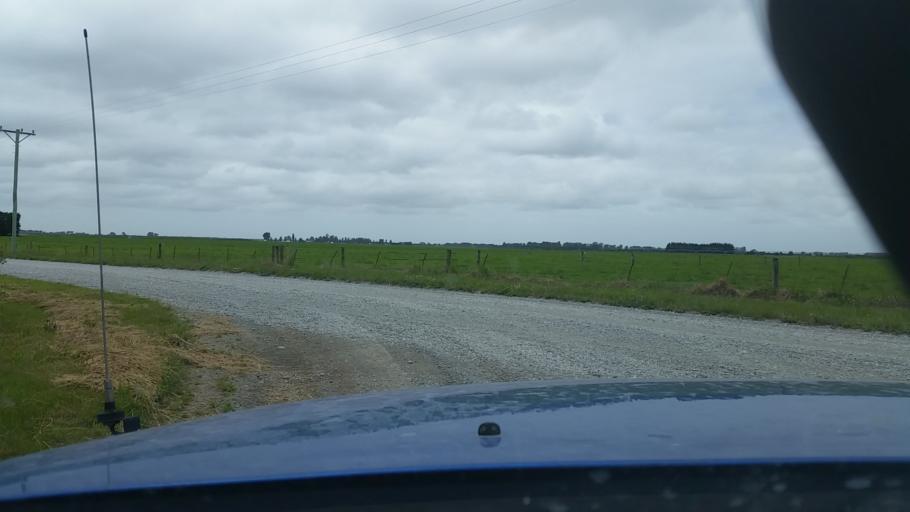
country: NZ
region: Canterbury
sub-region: Ashburton District
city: Tinwald
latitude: -44.0568
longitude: 171.5111
